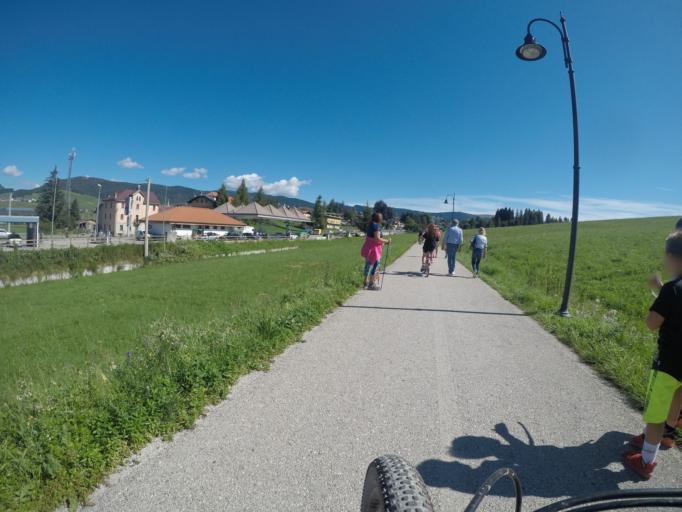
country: IT
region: Veneto
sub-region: Provincia di Vicenza
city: Asiago
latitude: 45.8694
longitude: 11.4984
